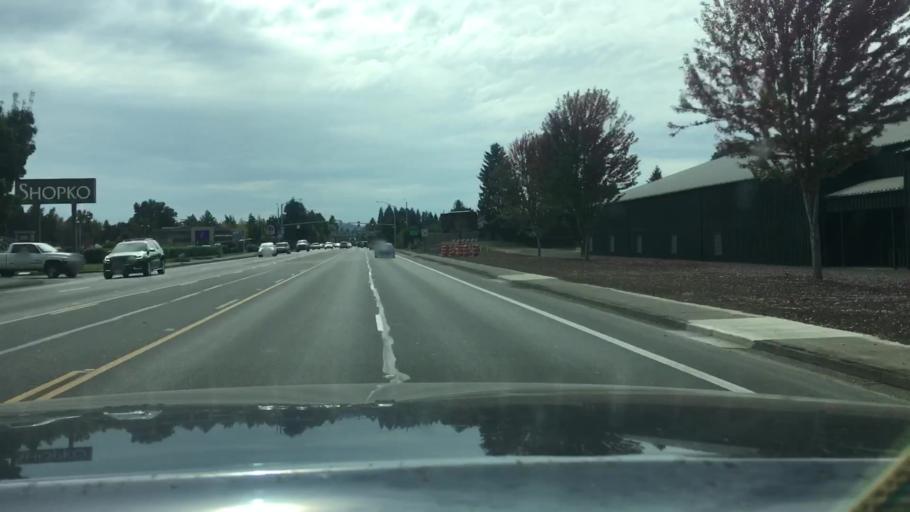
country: US
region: Oregon
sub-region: Lane County
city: Eugene
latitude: 44.0922
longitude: -123.0678
